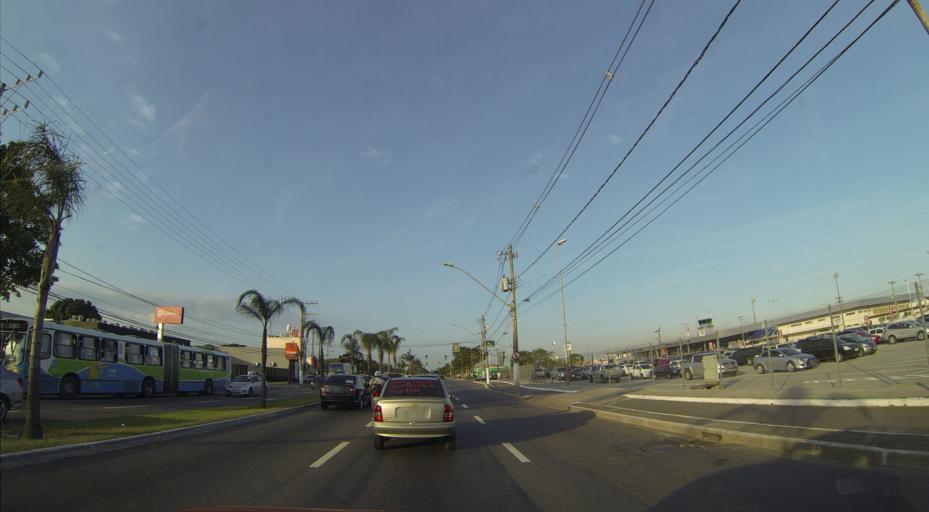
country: BR
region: Espirito Santo
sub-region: Vila Velha
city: Vila Velha
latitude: -20.2573
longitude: -40.2908
